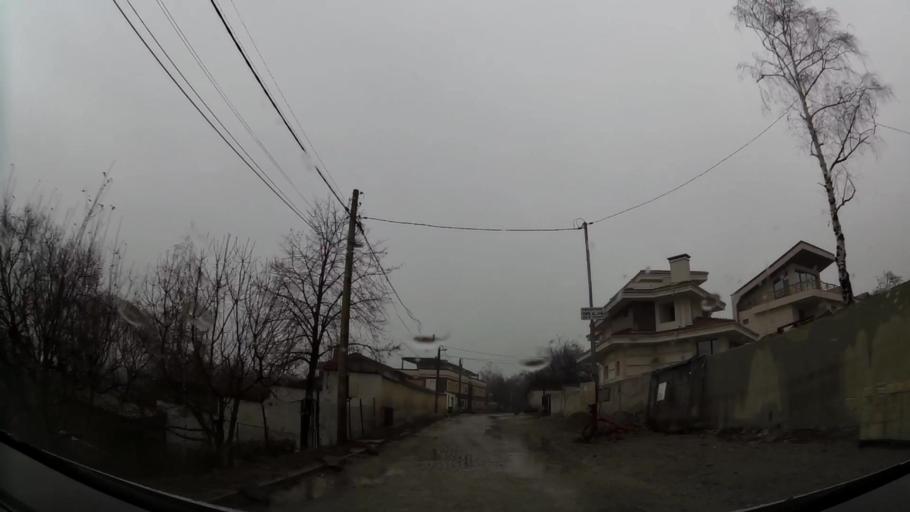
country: BG
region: Sofia-Capital
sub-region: Stolichna Obshtina
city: Sofia
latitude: 42.6285
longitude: 23.3611
